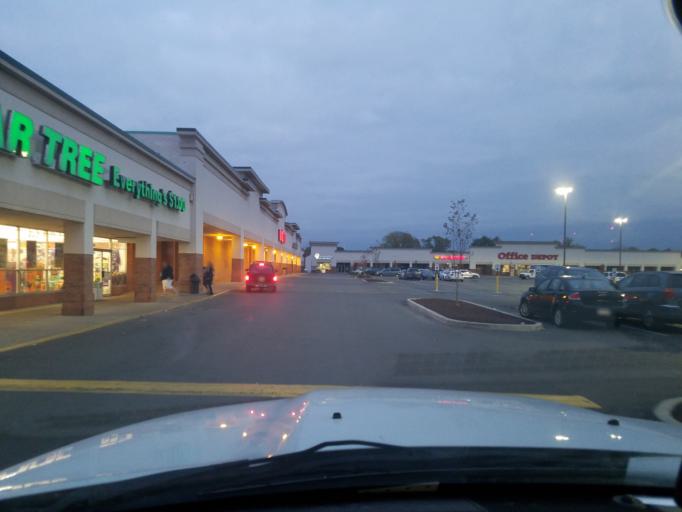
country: US
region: Indiana
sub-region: Floyd County
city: New Albany
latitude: 38.3061
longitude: -85.8394
